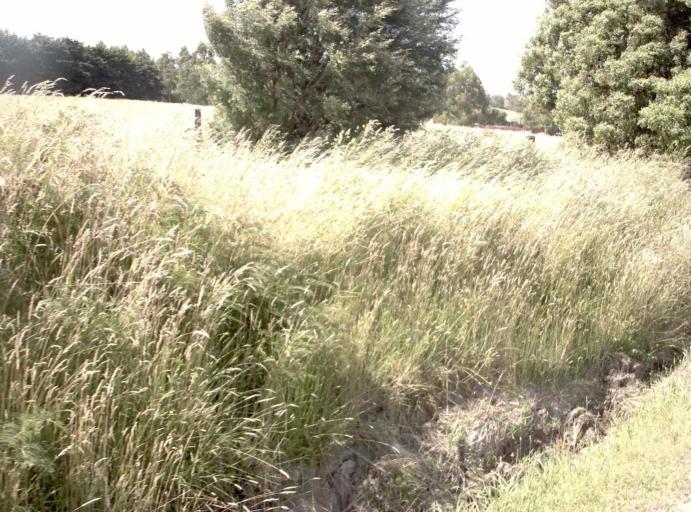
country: AU
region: Victoria
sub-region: Latrobe
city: Morwell
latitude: -38.1530
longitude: 146.4365
